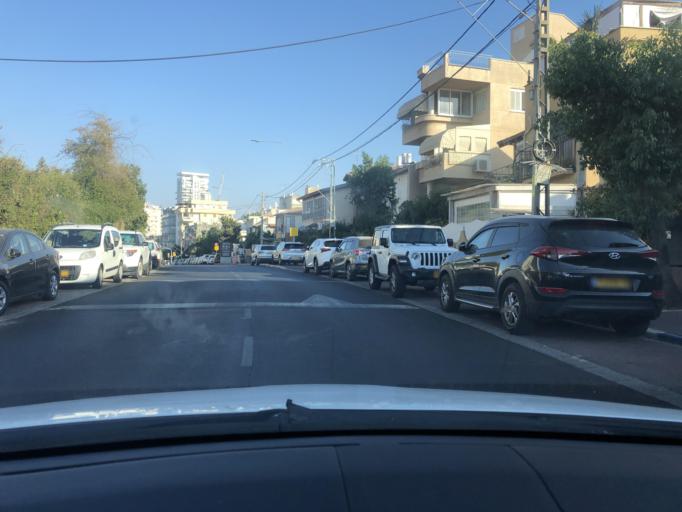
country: IL
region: Tel Aviv
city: Giv`atayim
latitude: 32.0622
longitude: 34.8238
